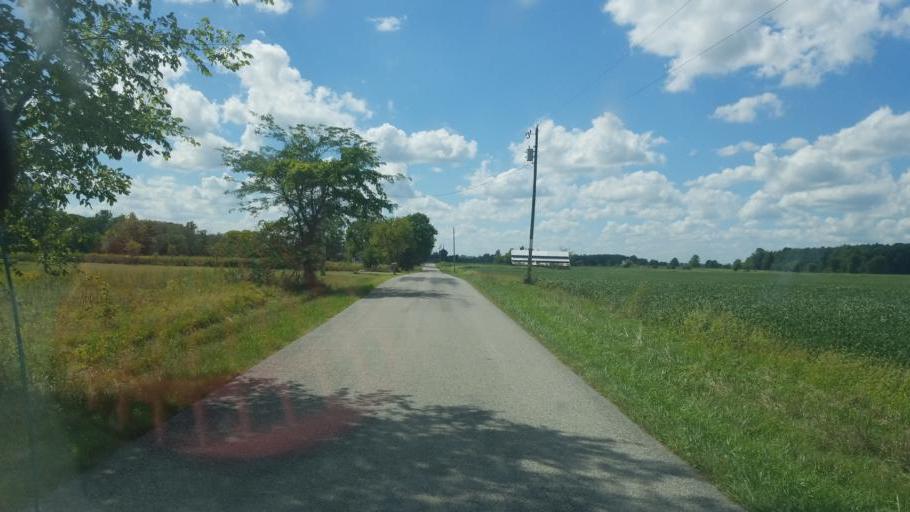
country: US
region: Ohio
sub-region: Marion County
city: Prospect
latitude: 40.3724
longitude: -83.2192
